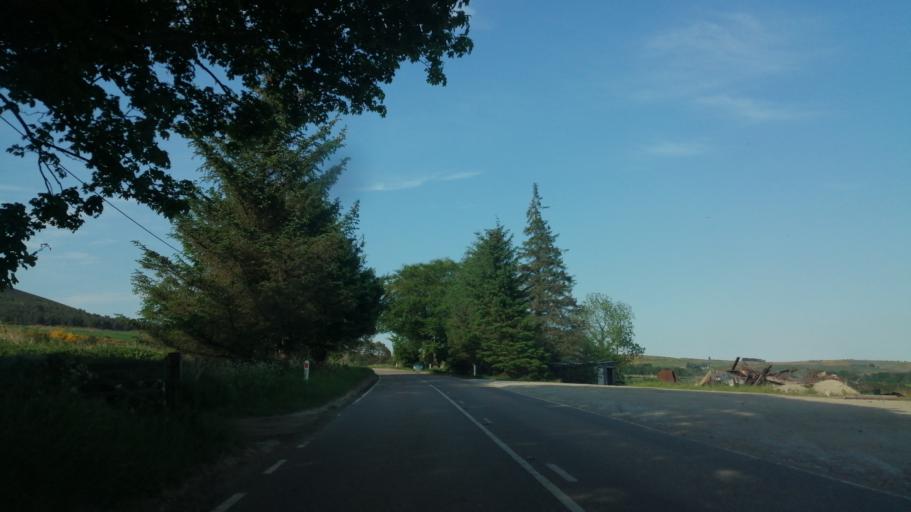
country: GB
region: Scotland
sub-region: Aberdeenshire
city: Huntly
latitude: 57.5673
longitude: -2.7861
